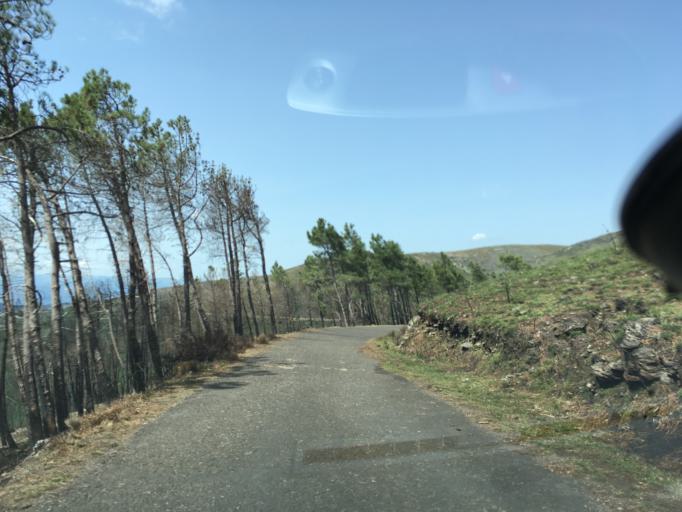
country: PT
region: Braga
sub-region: Celorico de Basto
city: Celorico de Basto
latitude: 41.2851
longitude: -7.9426
